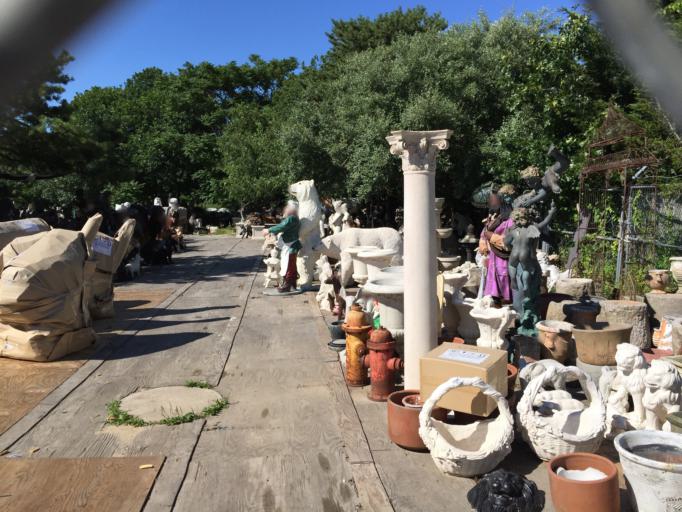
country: US
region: New York
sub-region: Suffolk County
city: Shinnecock Hills
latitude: 40.8952
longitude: -72.4501
